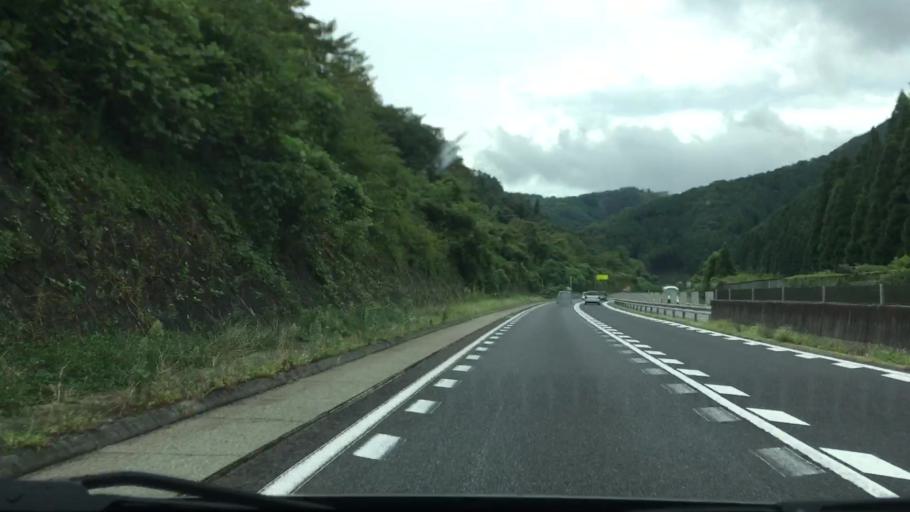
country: JP
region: Hyogo
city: Yamazakicho-nakabirose
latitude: 35.0440
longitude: 134.4646
